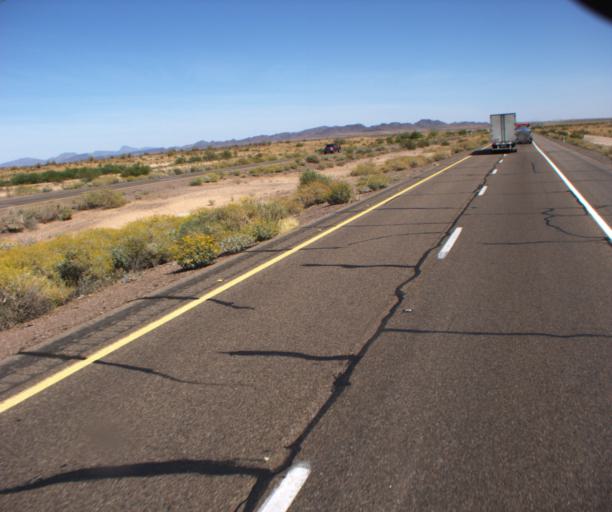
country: US
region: Arizona
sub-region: Maricopa County
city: Gila Bend
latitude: 32.8741
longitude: -113.1267
